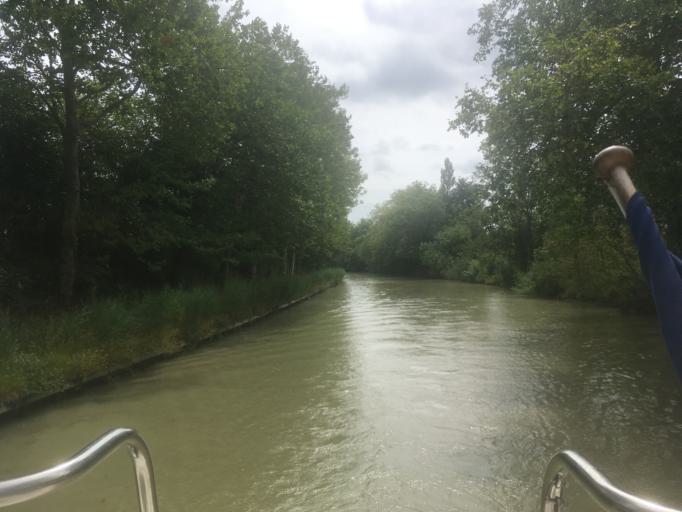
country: FR
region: Languedoc-Roussillon
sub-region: Departement de l'Aude
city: Villepinte
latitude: 43.2782
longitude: 2.0562
